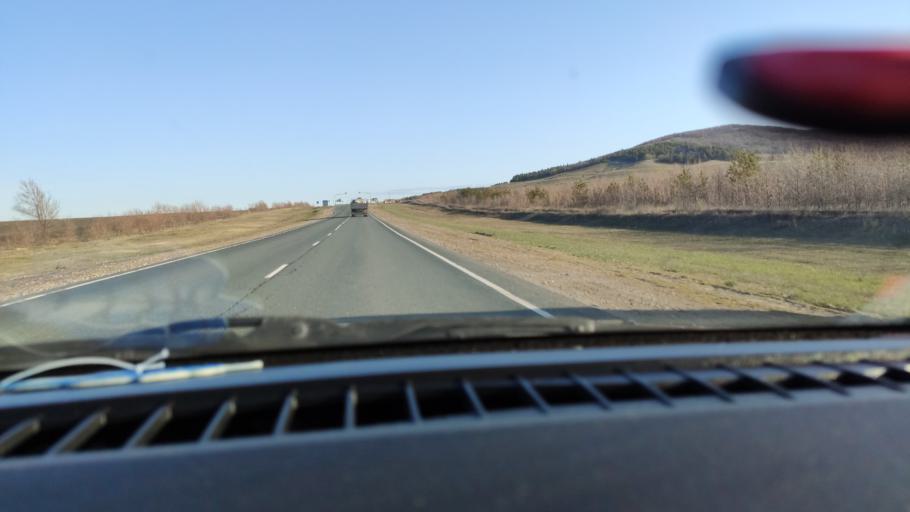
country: RU
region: Saratov
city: Alekseyevka
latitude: 52.2887
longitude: 47.9302
